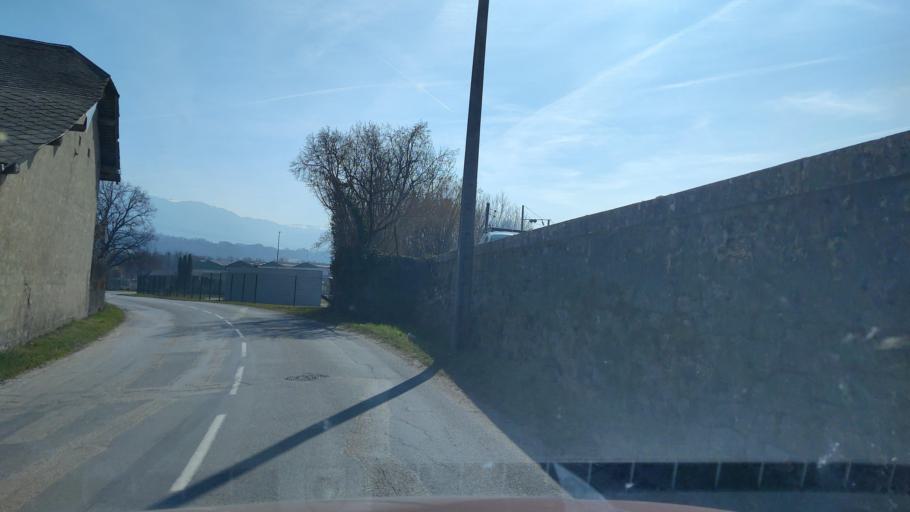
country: FR
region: Rhone-Alpes
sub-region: Departement de la Savoie
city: Albens
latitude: 45.7850
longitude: 5.9489
